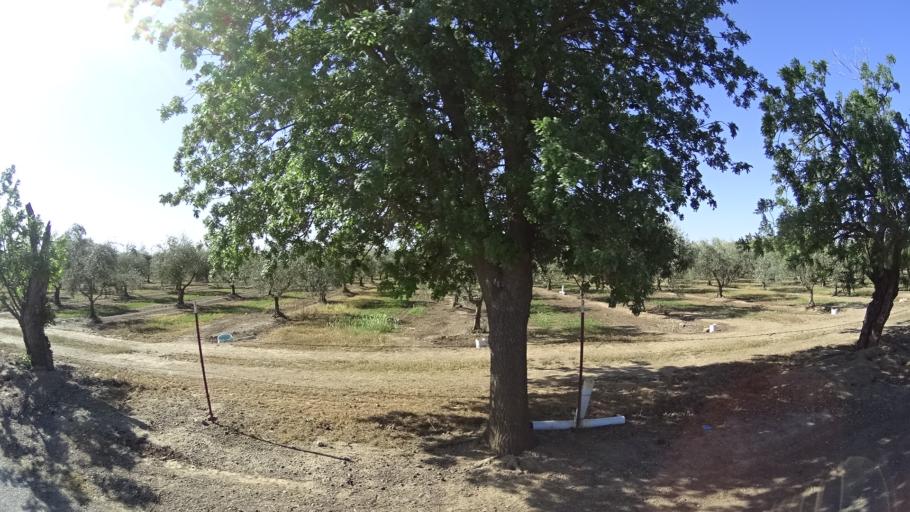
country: US
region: California
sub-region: Glenn County
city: Orland
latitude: 39.7542
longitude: -122.1660
